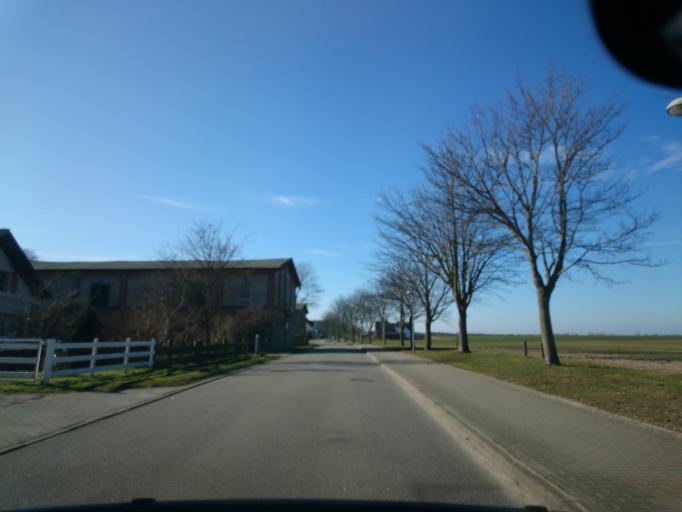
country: DE
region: Mecklenburg-Vorpommern
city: Borgerende-Rethwisch
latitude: 54.1426
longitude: 11.9224
